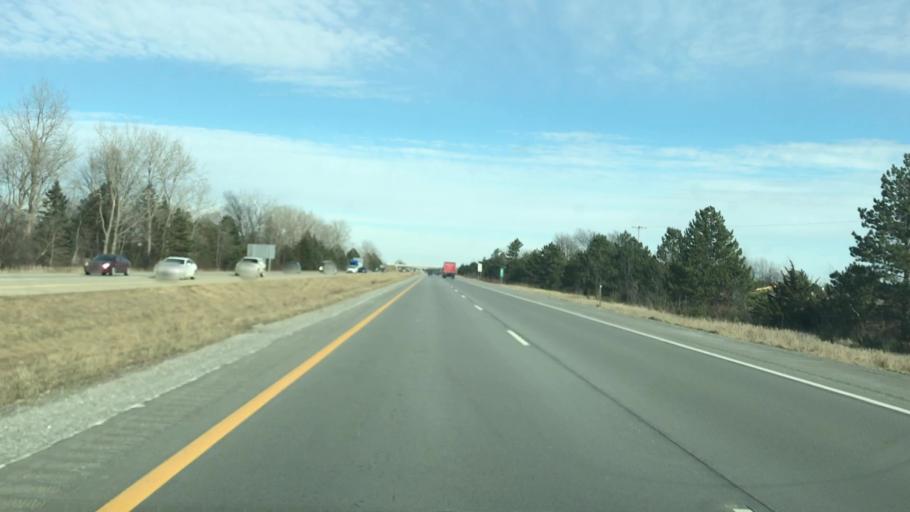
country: US
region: Michigan
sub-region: Bay County
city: Auburn
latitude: 43.5967
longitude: -84.0803
